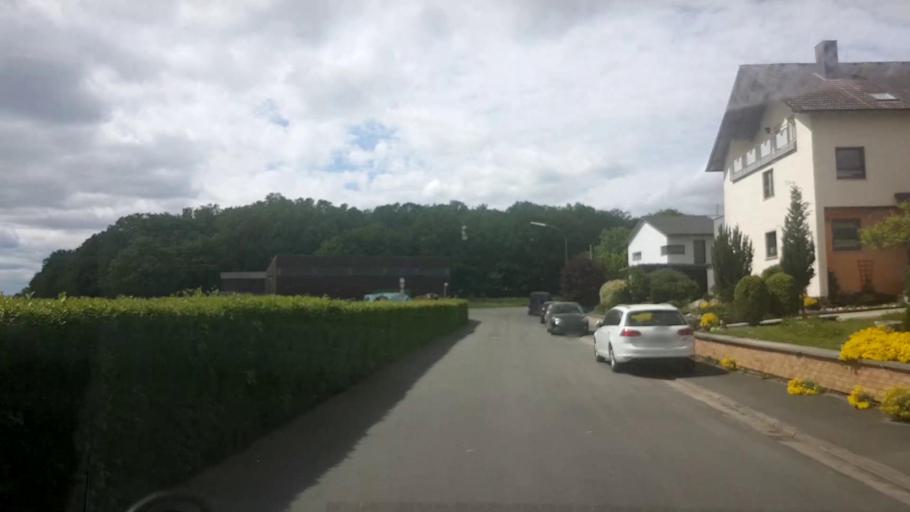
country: DE
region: Bavaria
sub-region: Upper Franconia
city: Bad Staffelstein
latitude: 50.1335
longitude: 11.0220
